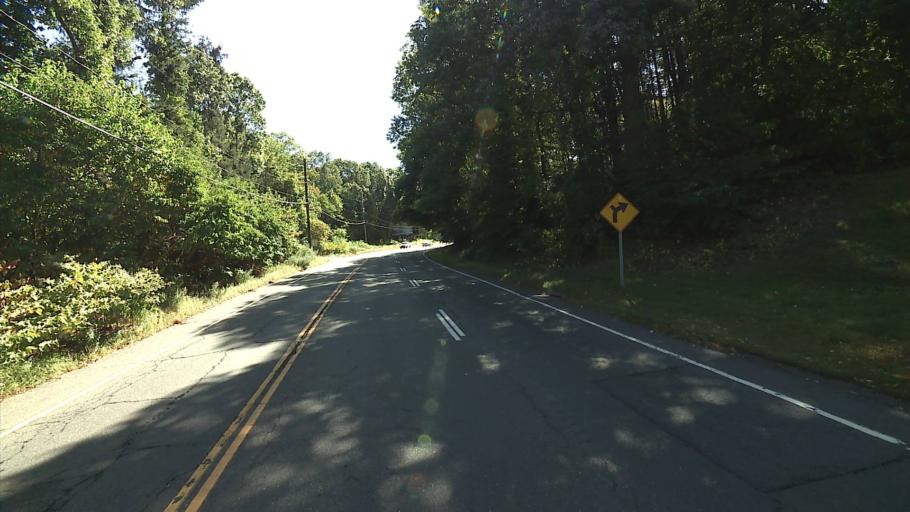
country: US
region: Connecticut
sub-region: New Haven County
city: Waterbury
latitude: 41.5359
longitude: -73.0119
